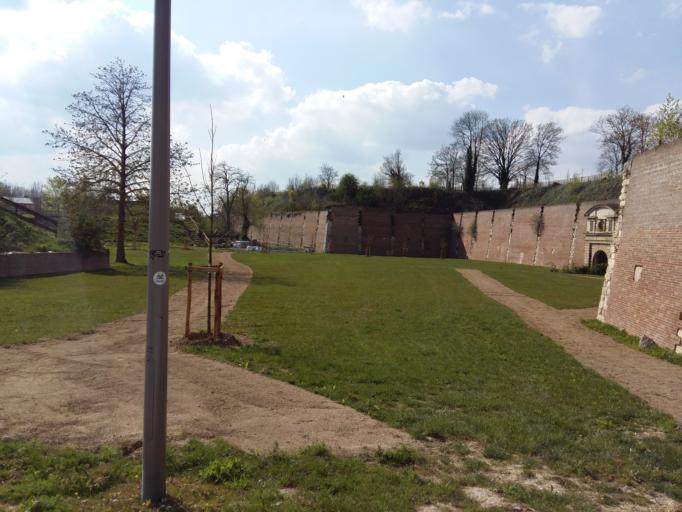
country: FR
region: Picardie
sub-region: Departement de la Somme
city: Amiens
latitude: 49.9029
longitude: 2.2997
